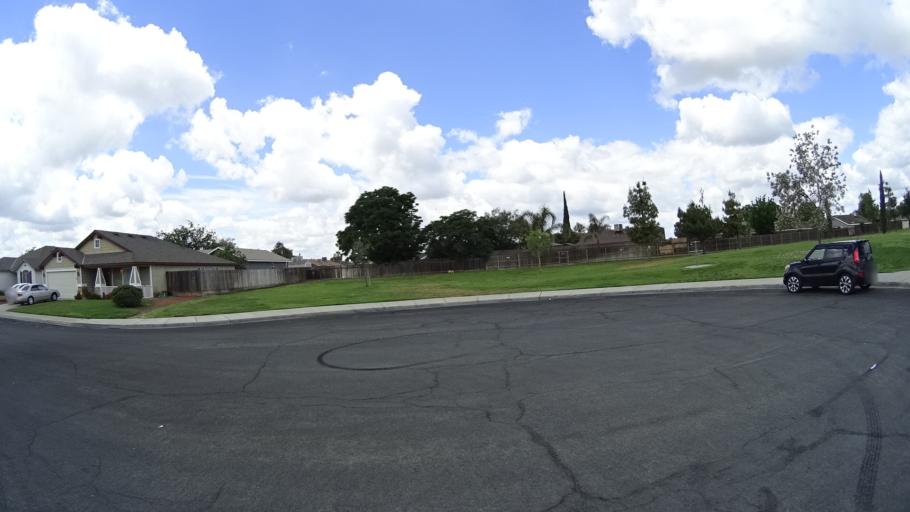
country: US
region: California
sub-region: Kings County
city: Hanford
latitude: 36.3464
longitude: -119.6274
